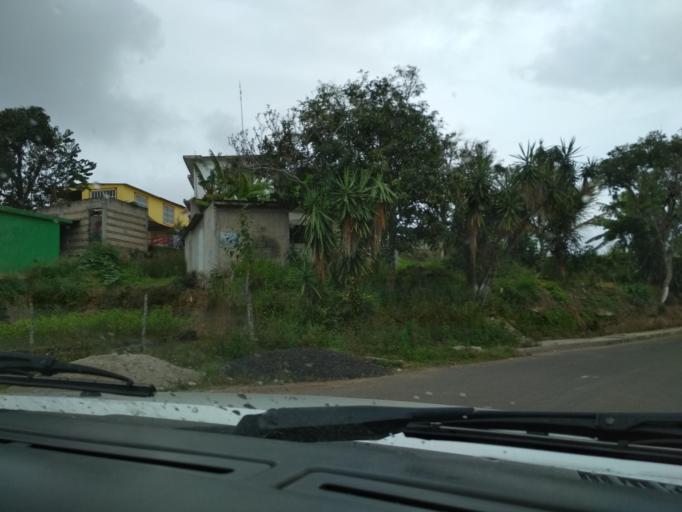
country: MX
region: Veracruz
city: El Castillo
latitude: 19.5345
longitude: -96.8155
